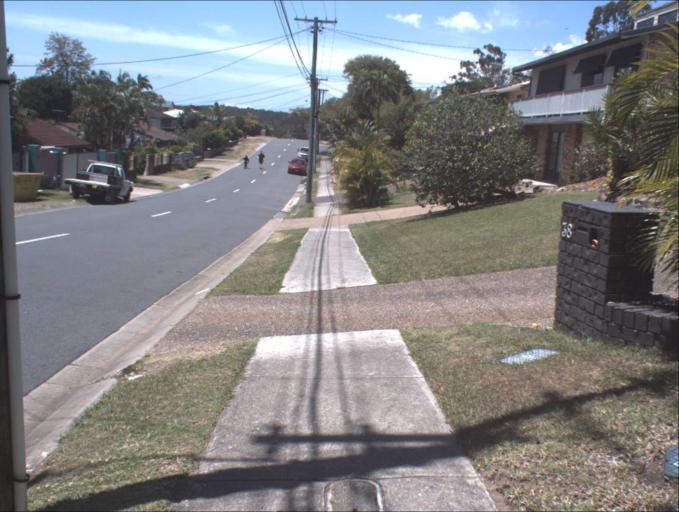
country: AU
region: Queensland
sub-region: Logan
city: Springwood
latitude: -27.6013
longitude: 153.1343
